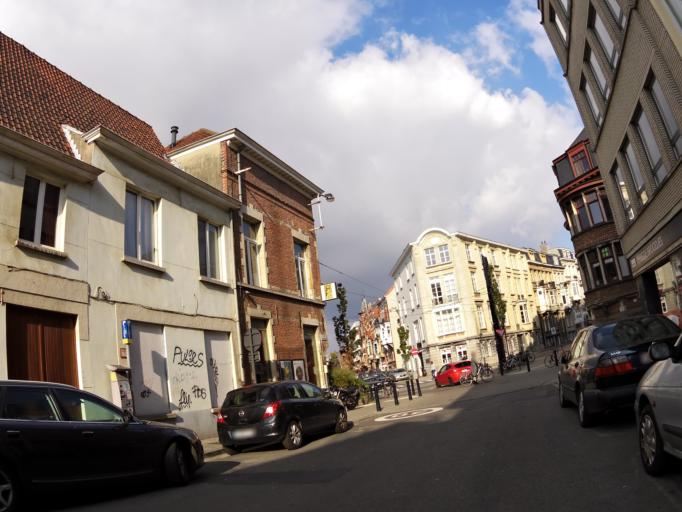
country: BE
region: Flanders
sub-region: Provincie Oost-Vlaanderen
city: Gent
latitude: 51.0498
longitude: 3.7170
